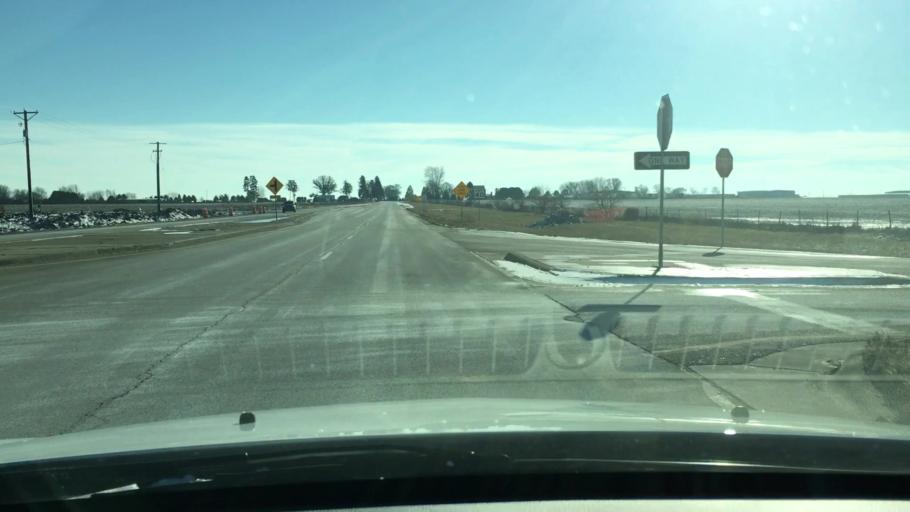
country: US
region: Illinois
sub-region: Ogle County
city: Rochelle
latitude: 41.8989
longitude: -89.0684
